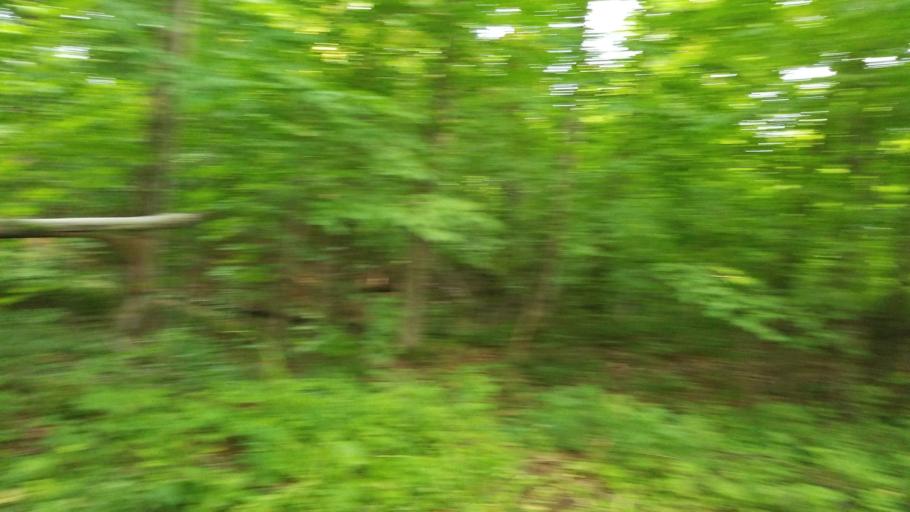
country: US
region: New York
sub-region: St. Lawrence County
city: Gouverneur
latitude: 44.1610
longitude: -75.3734
